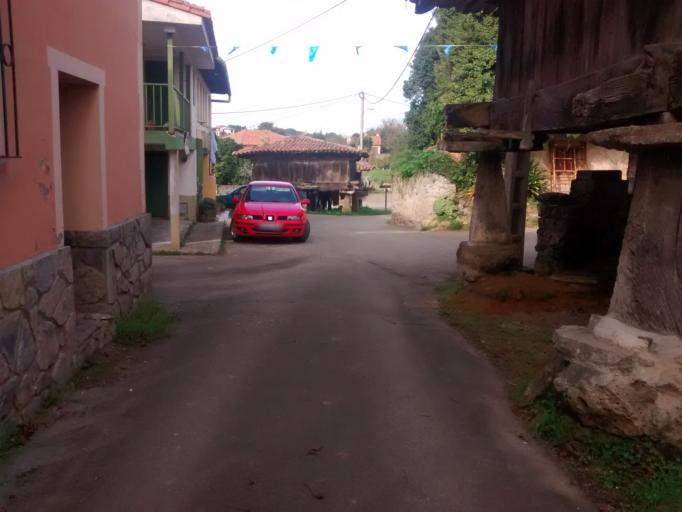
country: ES
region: Asturias
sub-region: Province of Asturias
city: Colunga
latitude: 43.4668
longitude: -5.2390
